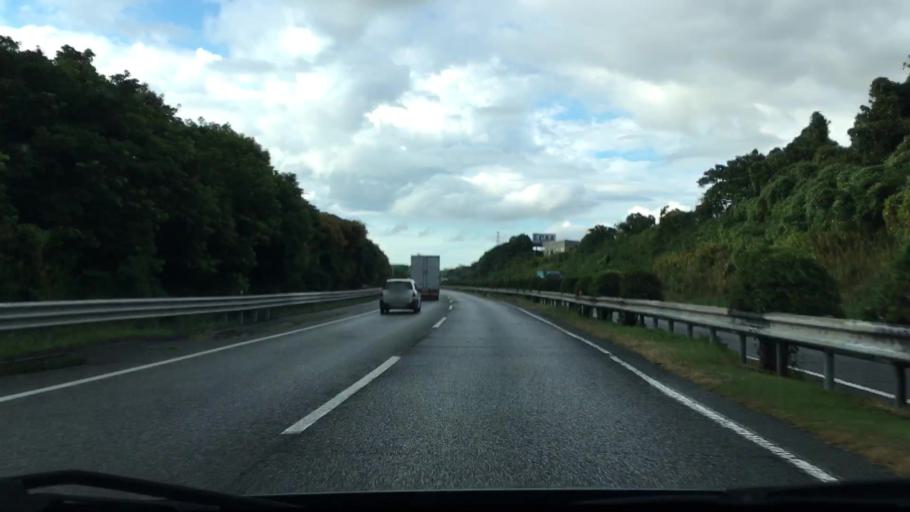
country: JP
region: Fukuoka
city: Koga
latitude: 33.6982
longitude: 130.4854
